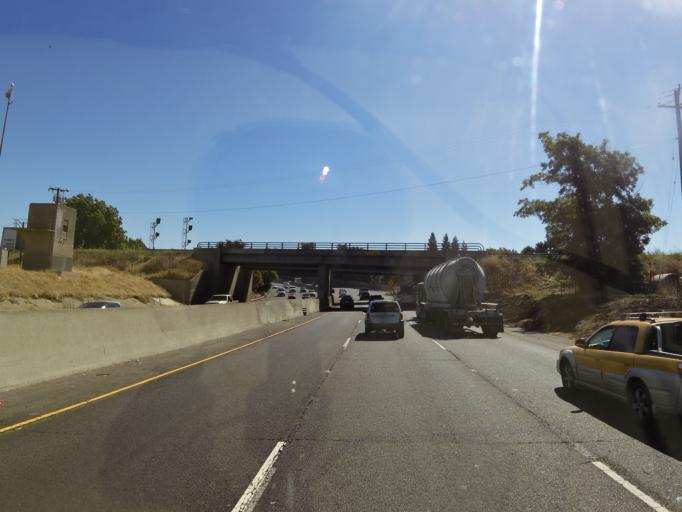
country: US
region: California
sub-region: Sacramento County
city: Sacramento
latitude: 38.5853
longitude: -121.4519
